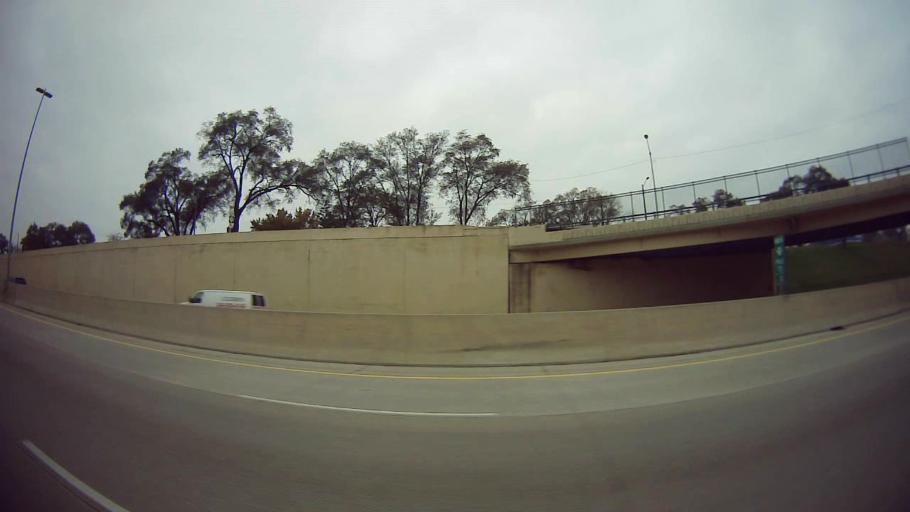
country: US
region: Michigan
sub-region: Oakland County
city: Southfield
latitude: 42.4431
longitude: -83.2196
